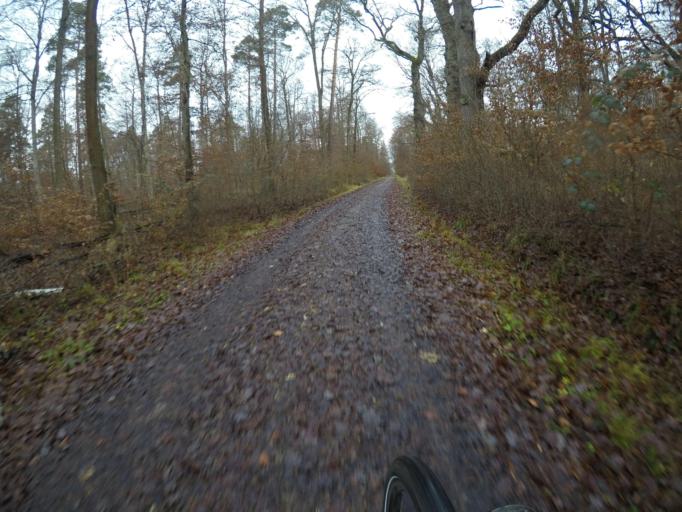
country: DE
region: Baden-Wuerttemberg
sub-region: Regierungsbezirk Stuttgart
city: Gerlingen
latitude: 48.7575
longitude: 9.0823
